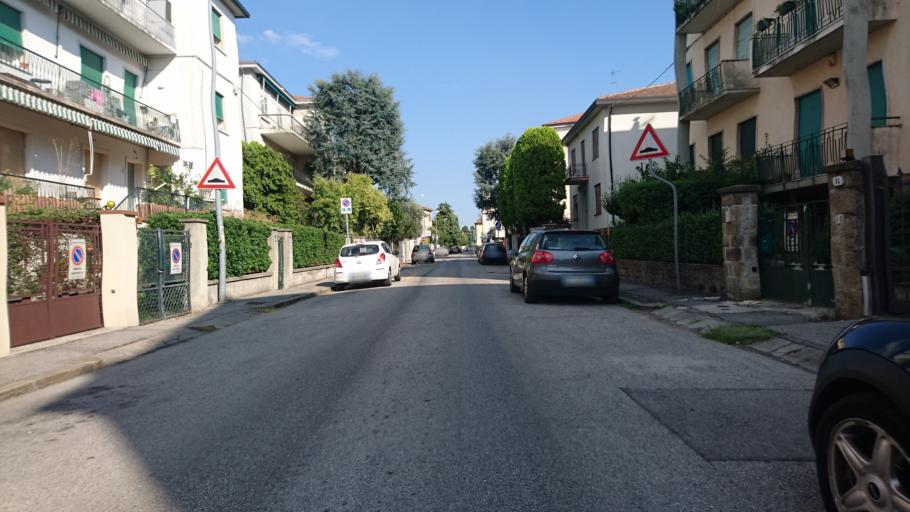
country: IT
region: Veneto
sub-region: Provincia di Padova
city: Padova
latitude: 45.4203
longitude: 11.8838
